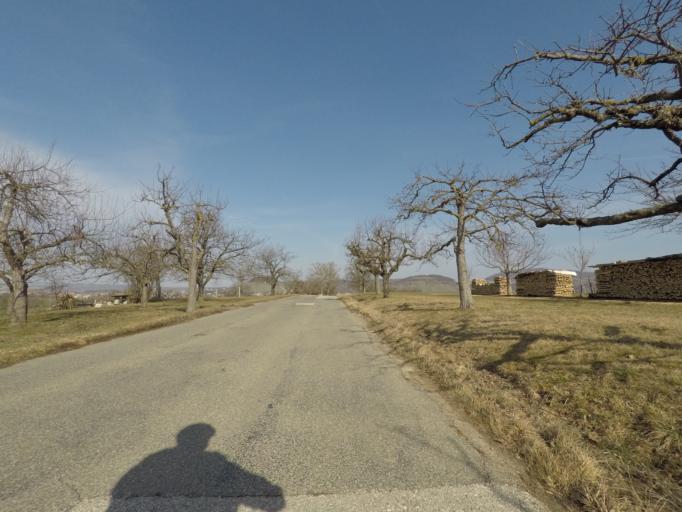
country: DE
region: Baden-Wuerttemberg
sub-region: Tuebingen Region
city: Metzingen
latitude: 48.5197
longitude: 9.2987
